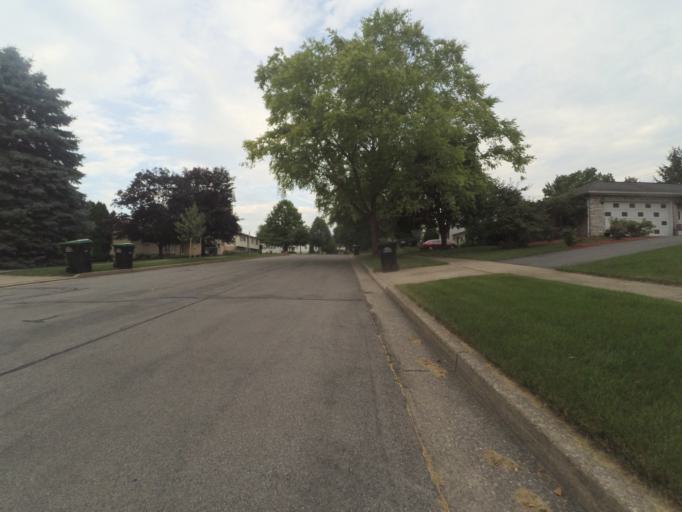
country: US
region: Pennsylvania
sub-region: Centre County
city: State College
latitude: 40.7766
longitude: -77.8674
